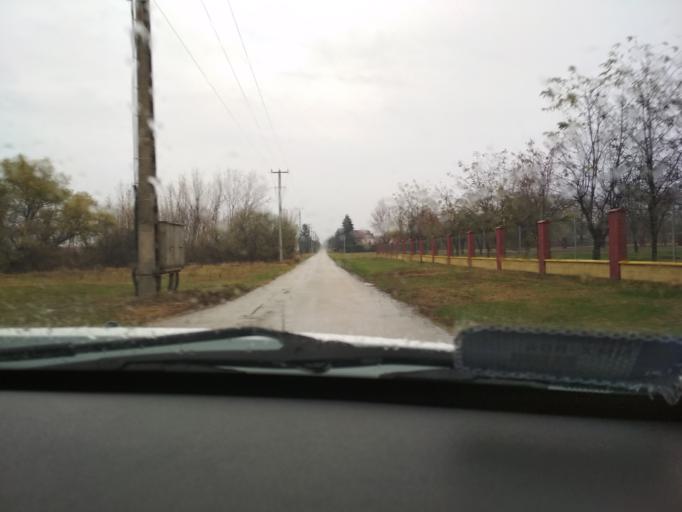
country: HU
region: Csongrad
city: Opusztaszer
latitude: 46.4354
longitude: 20.1288
